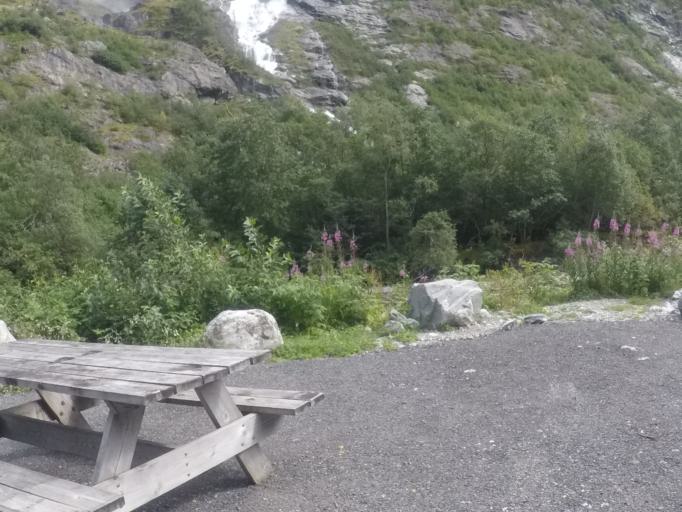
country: NO
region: Sogn og Fjordane
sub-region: Stryn
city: Stryn
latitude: 61.7469
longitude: 7.0356
